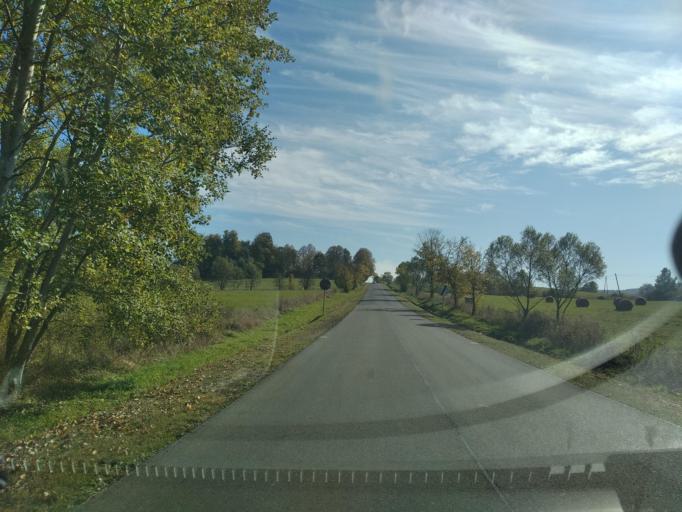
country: PL
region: Subcarpathian Voivodeship
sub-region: Powiat sanocki
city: Komancza
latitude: 49.3885
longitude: 21.9902
